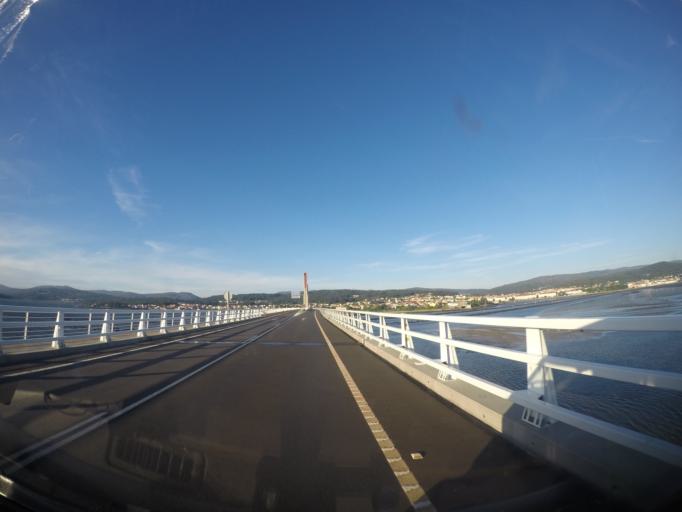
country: ES
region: Galicia
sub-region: Provincia da Coruna
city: Noia
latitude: 42.7912
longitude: -8.9060
